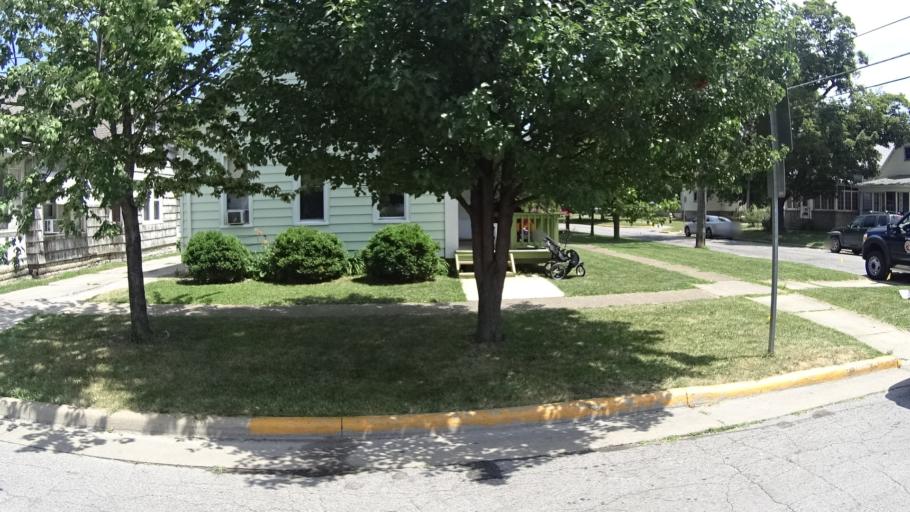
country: US
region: Ohio
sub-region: Erie County
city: Sandusky
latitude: 41.4414
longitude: -82.7082
